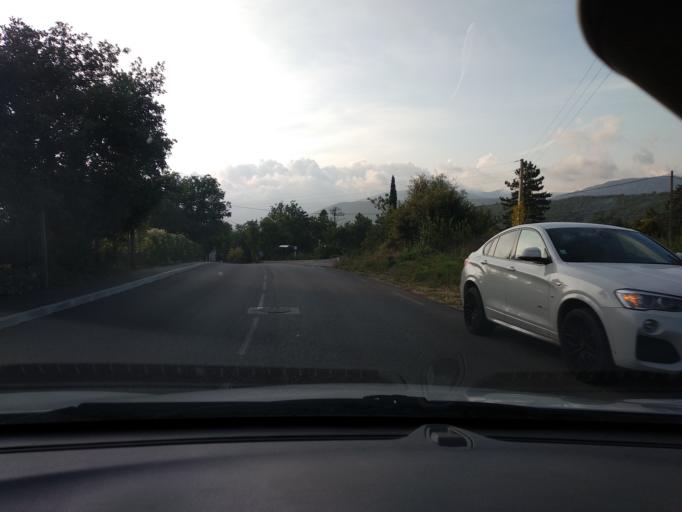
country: FR
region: Provence-Alpes-Cote d'Azur
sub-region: Departement des Alpes-Maritimes
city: Saint-Cezaire-sur-Siagne
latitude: 43.6520
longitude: 6.8144
